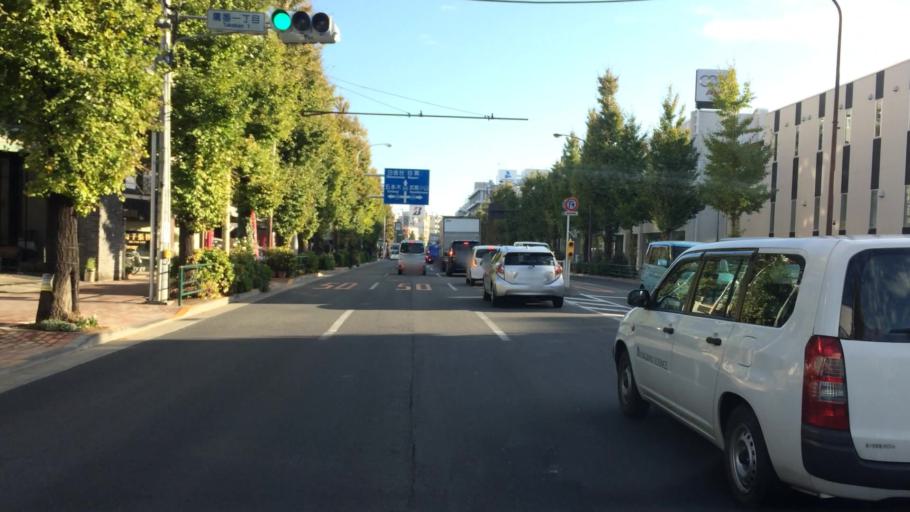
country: JP
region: Tokyo
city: Tokyo
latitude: 35.6266
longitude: 139.6911
